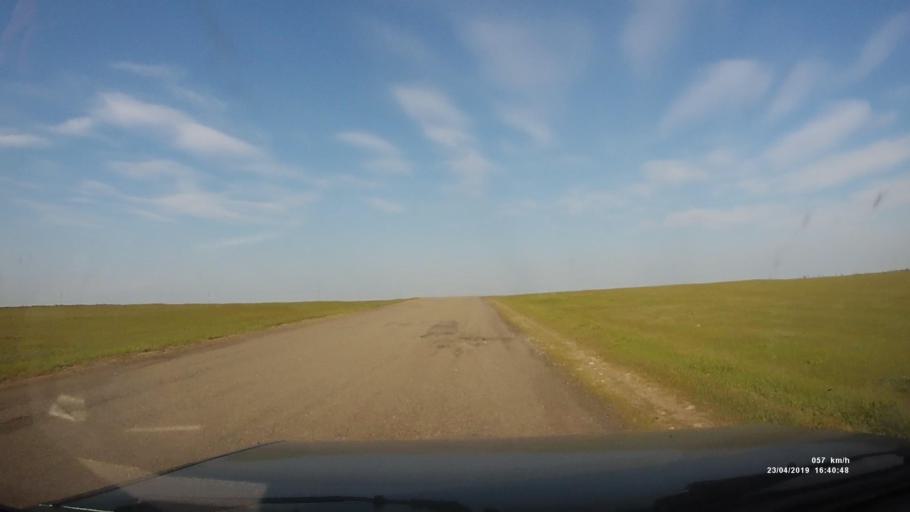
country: RU
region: Kalmykiya
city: Priyutnoye
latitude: 46.3440
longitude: 43.1804
